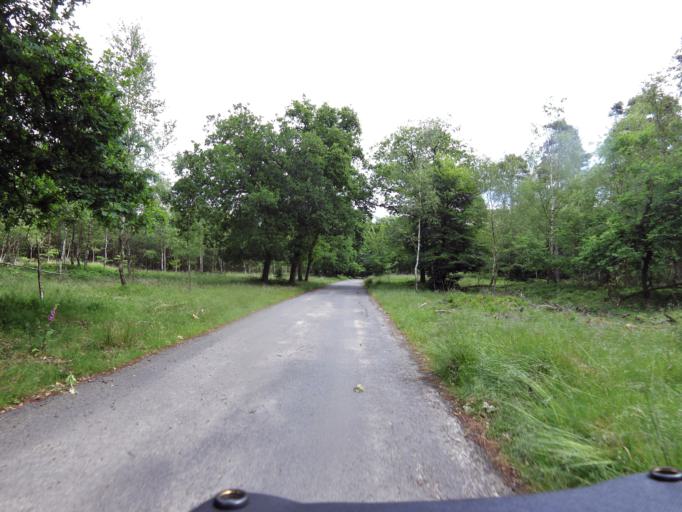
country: NL
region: Gelderland
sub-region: Gemeente Epe
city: Vaassen
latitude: 52.3079
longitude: 5.8722
